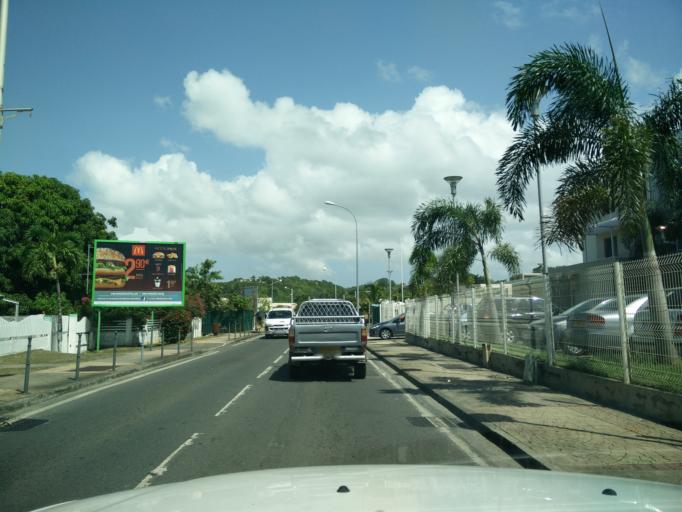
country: GP
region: Guadeloupe
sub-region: Guadeloupe
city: Le Gosier
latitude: 16.2136
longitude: -61.5008
